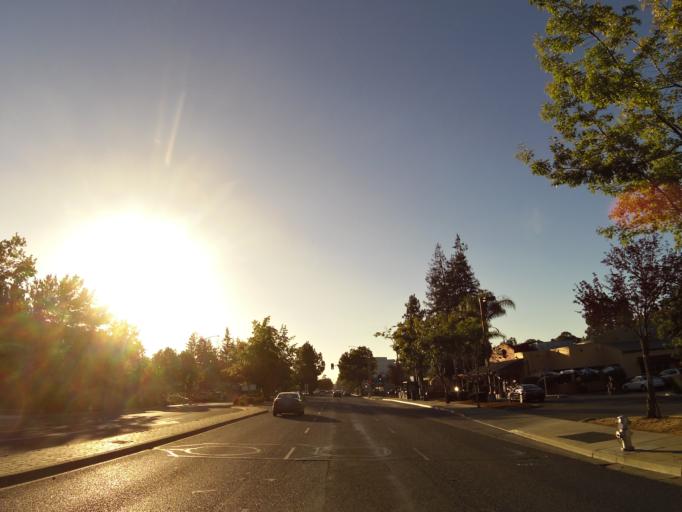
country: US
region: California
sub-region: Santa Clara County
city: Los Altos
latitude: 37.3959
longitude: -122.1021
